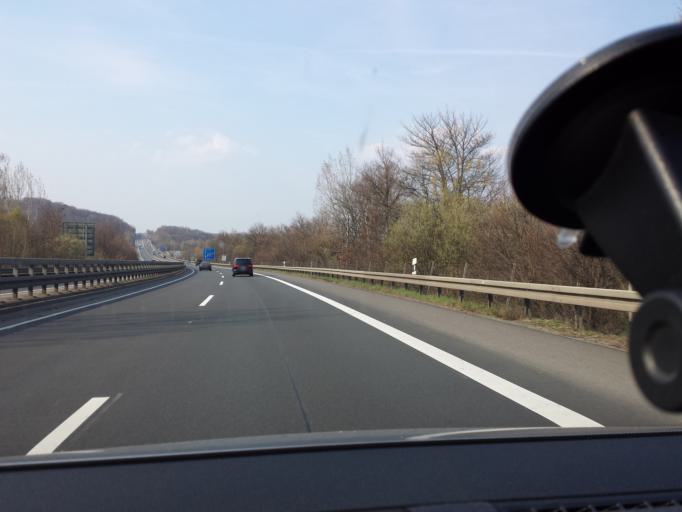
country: DE
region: Lower Saxony
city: Vienenburg
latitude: 51.9513
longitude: 10.5838
